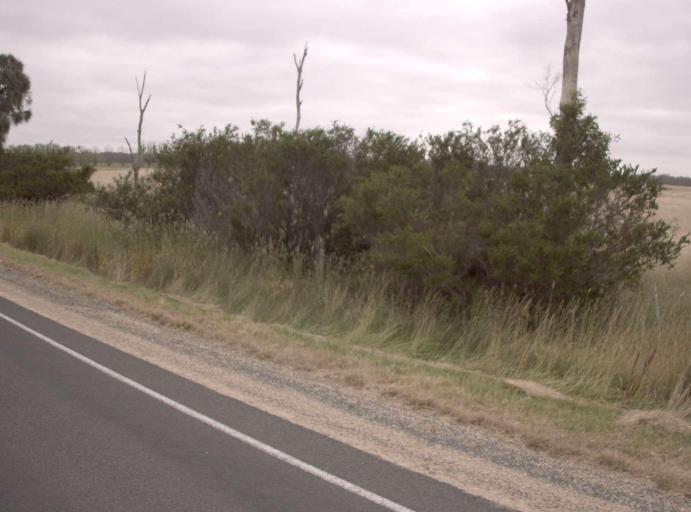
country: AU
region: Victoria
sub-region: Wellington
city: Sale
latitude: -38.0867
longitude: 146.9875
